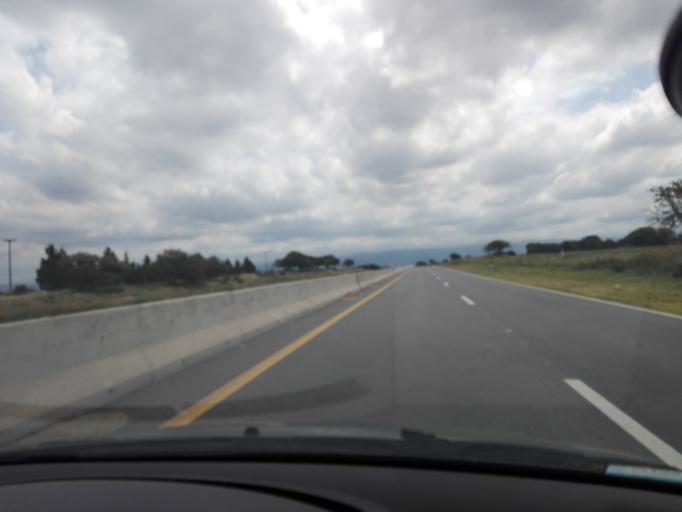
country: AR
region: Cordoba
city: Alta Gracia
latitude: -31.6521
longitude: -64.3239
